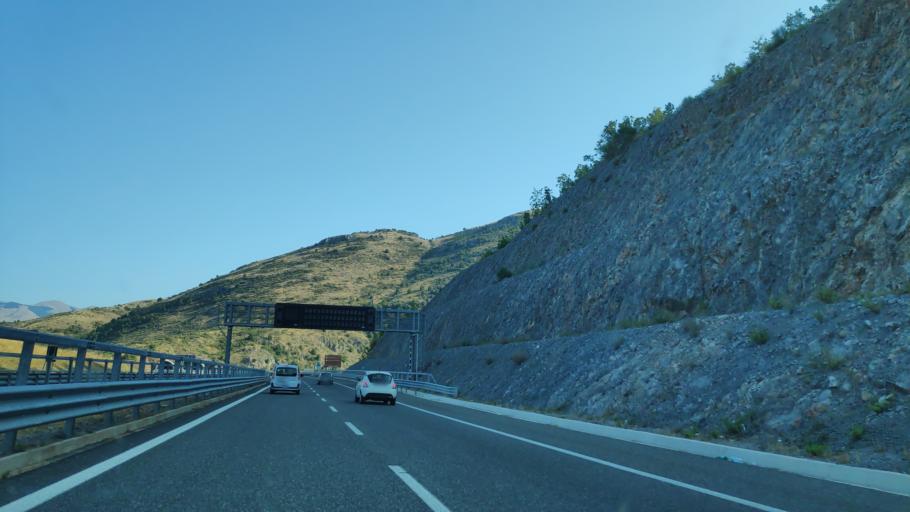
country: IT
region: Basilicate
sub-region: Provincia di Potenza
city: Lauria
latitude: 40.0321
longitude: 15.8746
